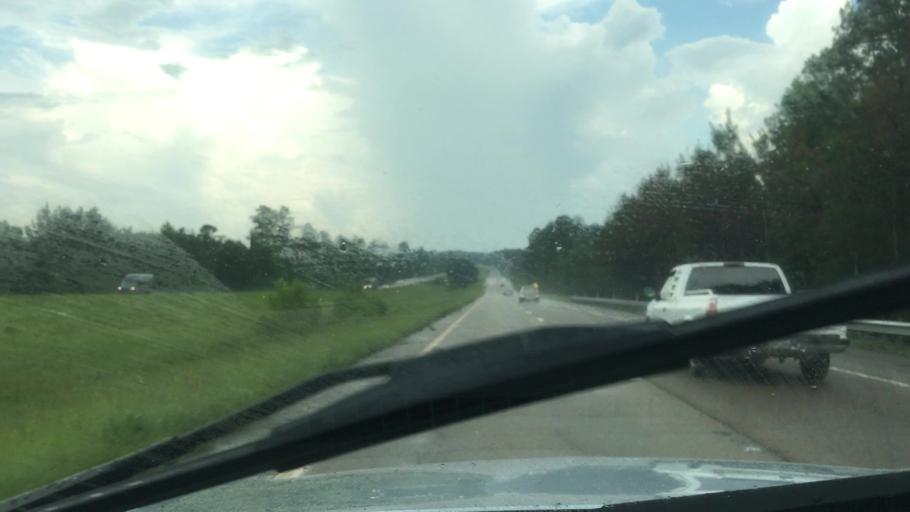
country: US
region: Mississippi
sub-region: Lamar County
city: Purvis
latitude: 31.1645
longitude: -89.3544
